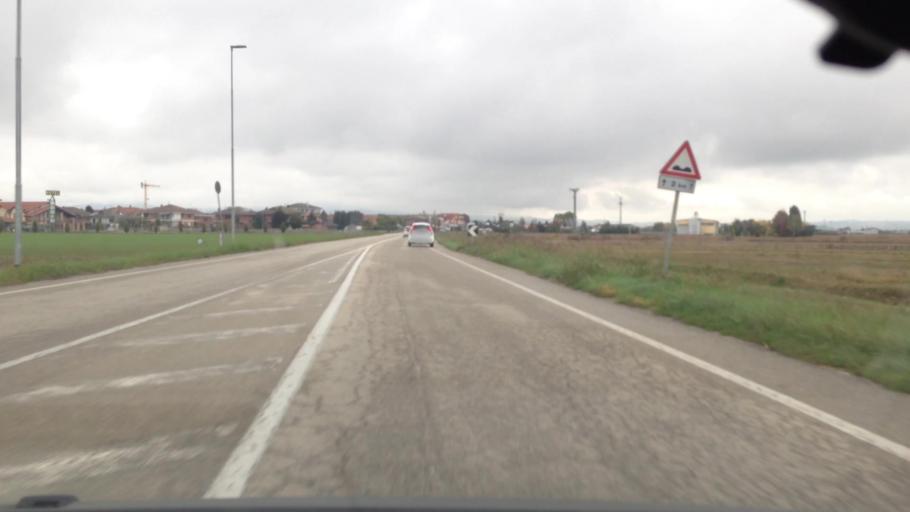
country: IT
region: Piedmont
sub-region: Provincia di Torino
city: Riva Presso Chieri
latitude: 44.9765
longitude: 7.8823
